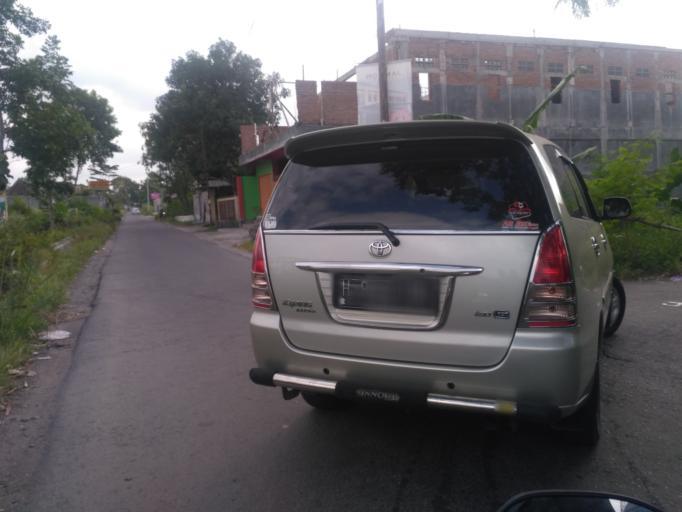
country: ID
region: Daerah Istimewa Yogyakarta
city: Yogyakarta
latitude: -7.7706
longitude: 110.3588
